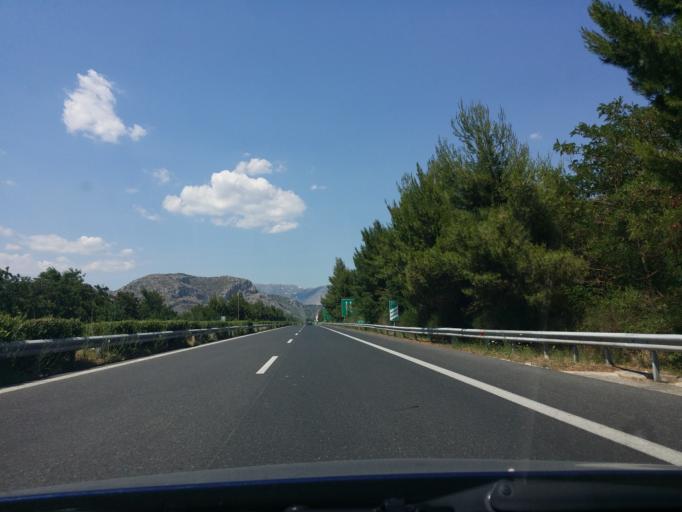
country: GR
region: Peloponnese
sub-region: Nomos Arkadias
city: Tripoli
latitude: 37.5741
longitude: 22.4292
